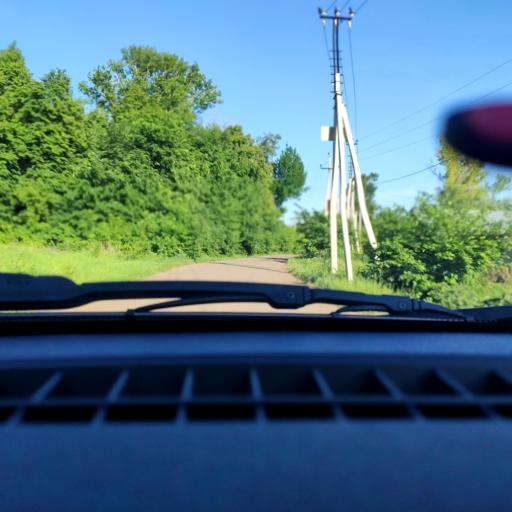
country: RU
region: Bashkortostan
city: Avdon
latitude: 54.4647
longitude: 55.8345
